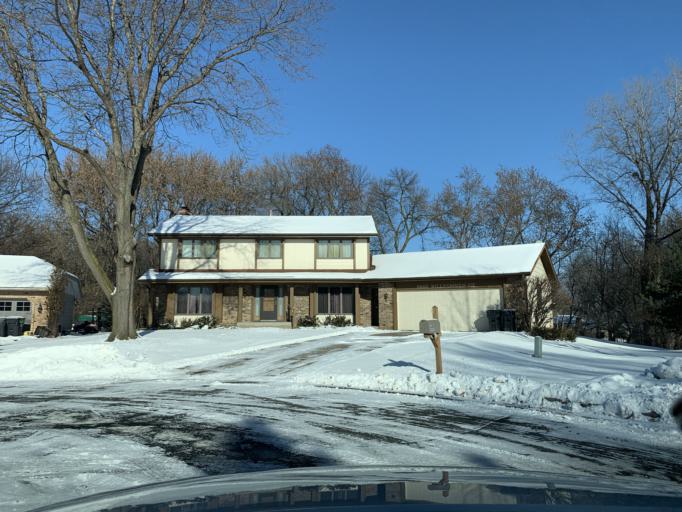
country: US
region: Minnesota
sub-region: Hennepin County
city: Edina
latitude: 44.8363
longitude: -93.3564
